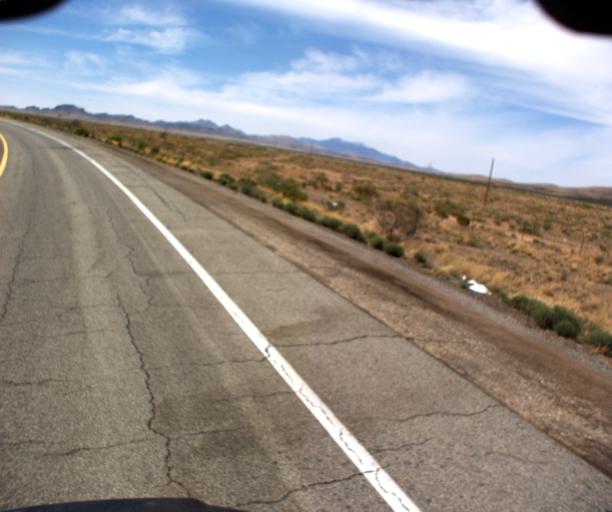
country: US
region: Arizona
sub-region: Cochise County
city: Willcox
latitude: 32.3627
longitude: -109.6189
